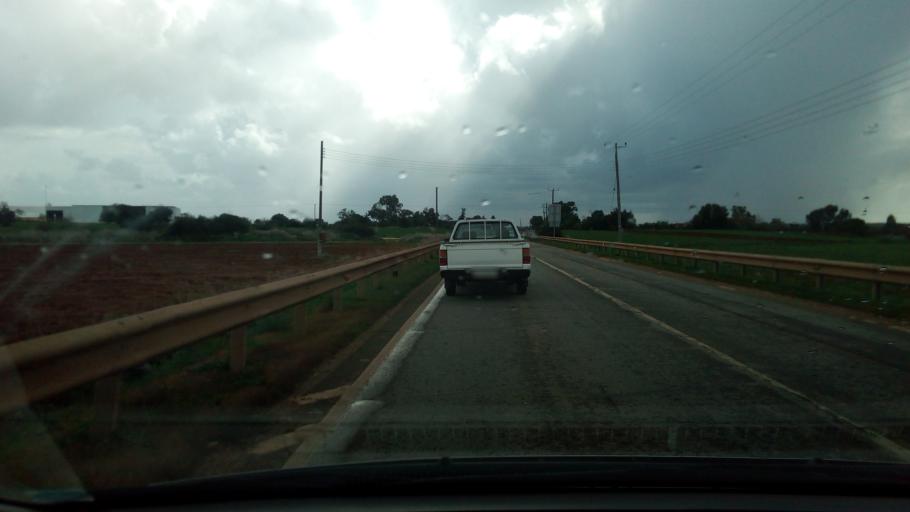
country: CY
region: Ammochostos
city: Liopetri
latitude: 34.9958
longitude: 33.8921
